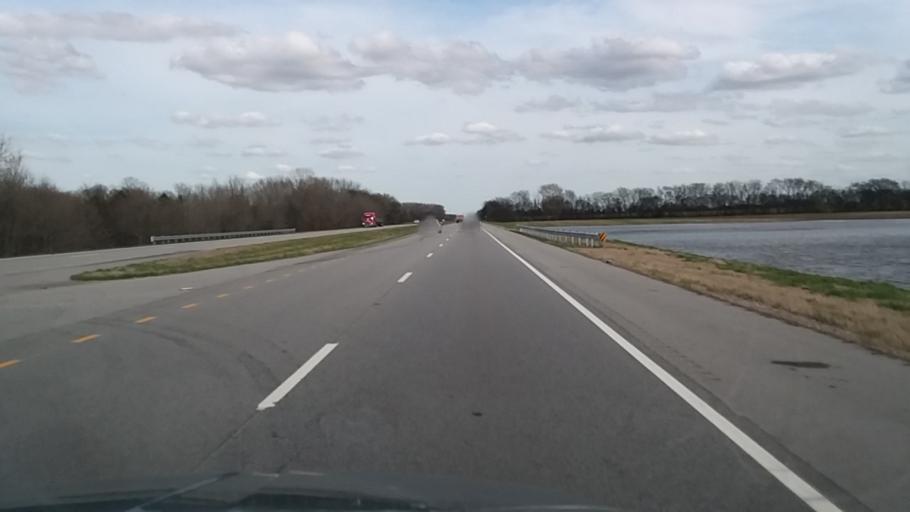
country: US
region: Alabama
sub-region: Lawrence County
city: Town Creek
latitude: 34.6836
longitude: -87.5158
